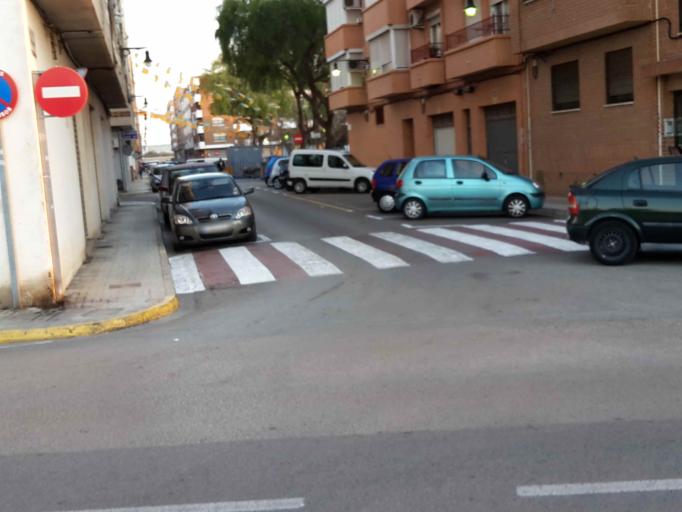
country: ES
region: Valencia
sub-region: Provincia de Valencia
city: Xirivella
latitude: 39.4660
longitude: -0.4370
